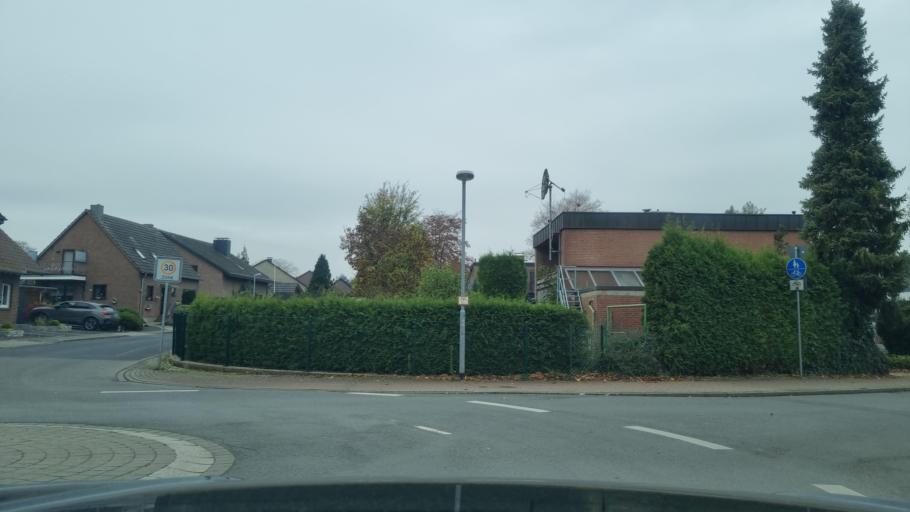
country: DE
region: North Rhine-Westphalia
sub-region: Regierungsbezirk Dusseldorf
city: Kranenburg
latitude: 51.7892
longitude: 6.0748
